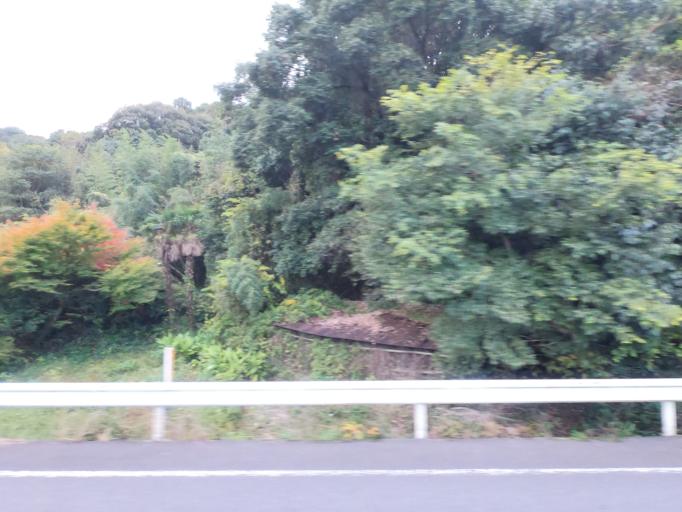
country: JP
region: Kumamoto
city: Minamata
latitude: 32.2592
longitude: 130.5100
